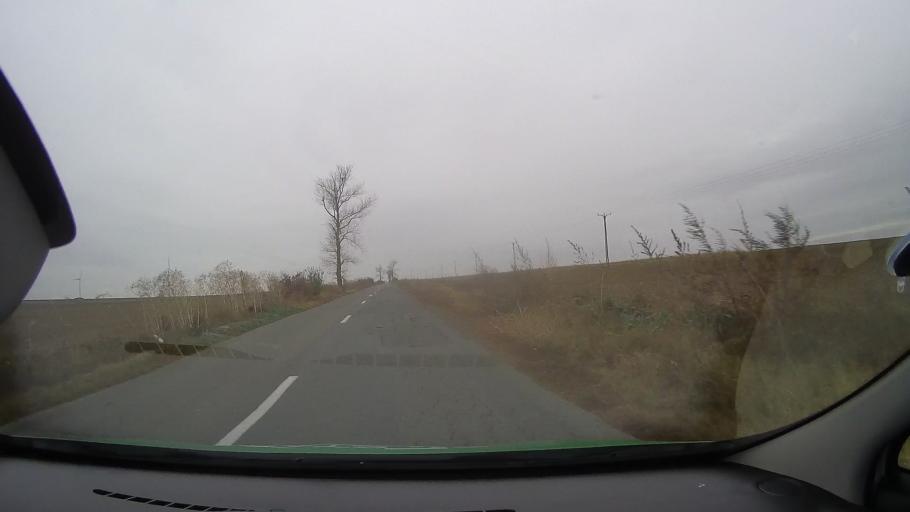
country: RO
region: Constanta
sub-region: Comuna Pantelimon
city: Pantelimon
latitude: 44.5624
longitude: 28.3206
